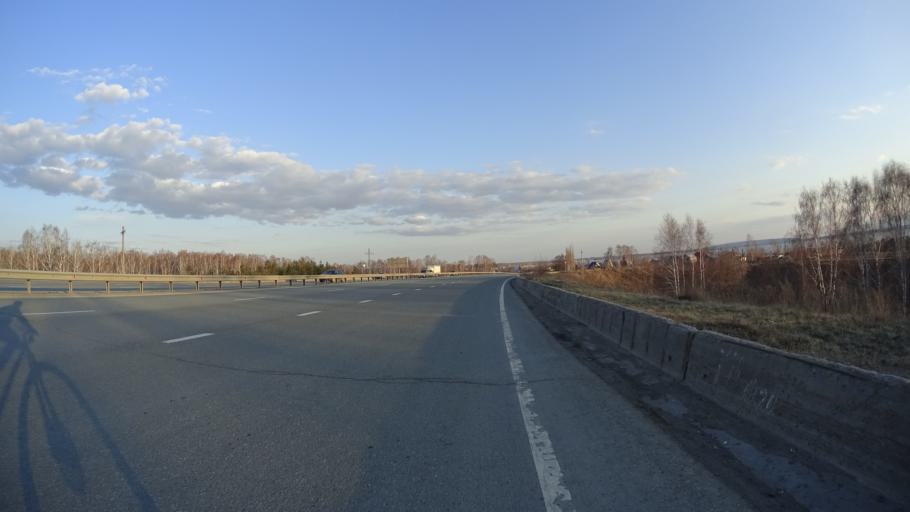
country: RU
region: Chelyabinsk
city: Novosineglazovskiy
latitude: 55.0386
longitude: 61.4407
